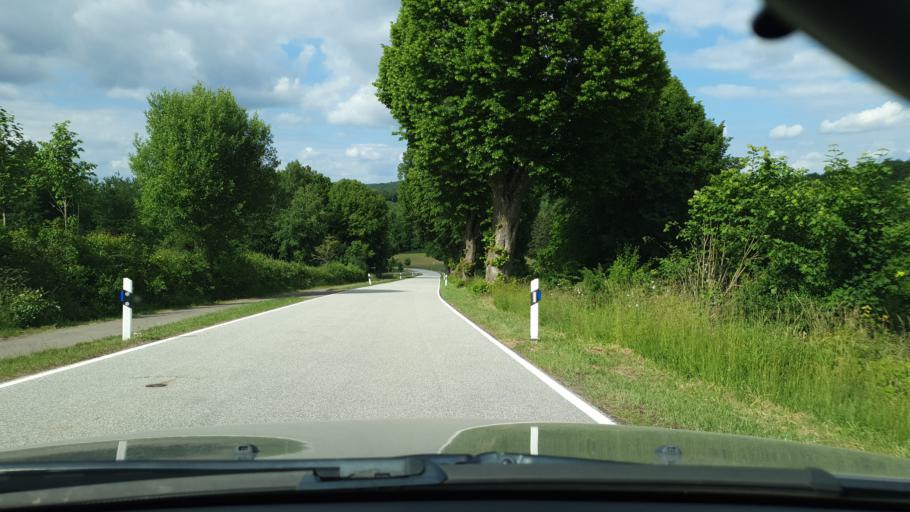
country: DE
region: Rheinland-Pfalz
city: Martinshohe
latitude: 49.3698
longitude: 7.4824
